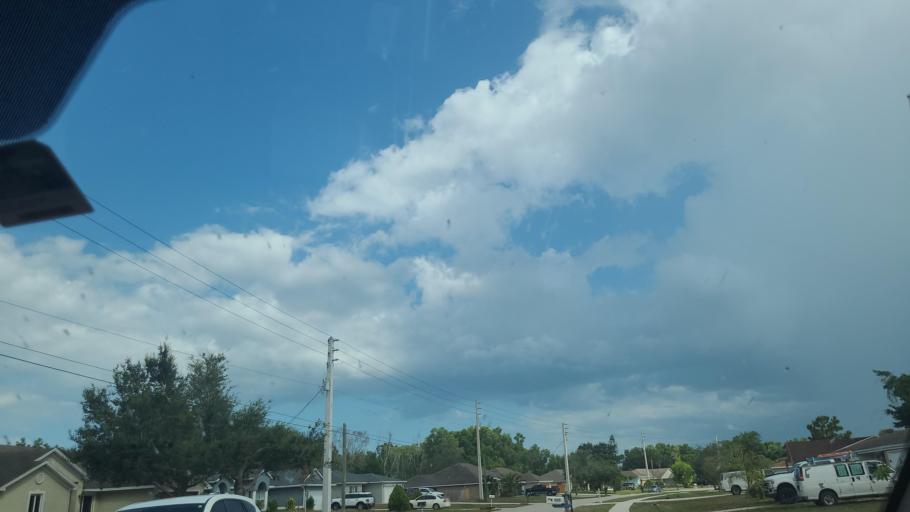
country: US
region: Florida
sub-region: Saint Lucie County
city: Port Saint Lucie
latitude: 27.2561
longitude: -80.3555
